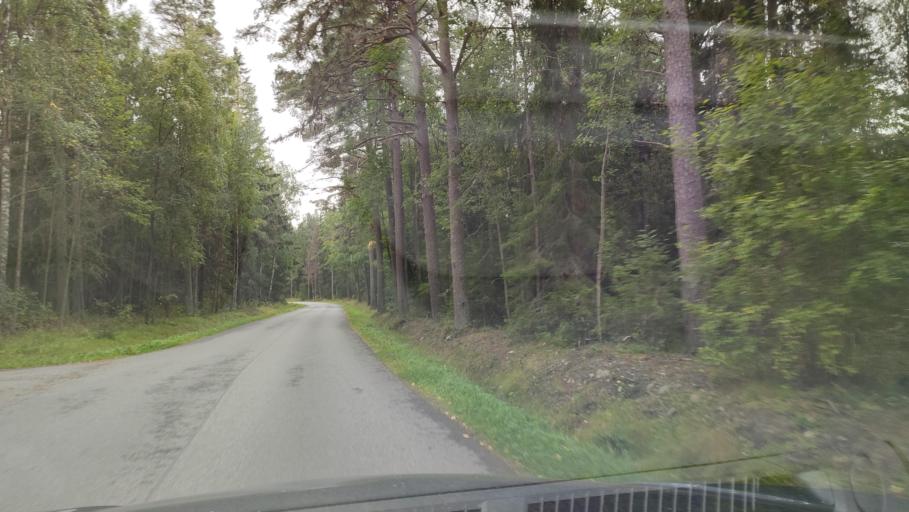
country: FI
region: Ostrobothnia
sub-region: Sydosterbotten
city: Kristinestad
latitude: 62.2583
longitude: 21.3580
